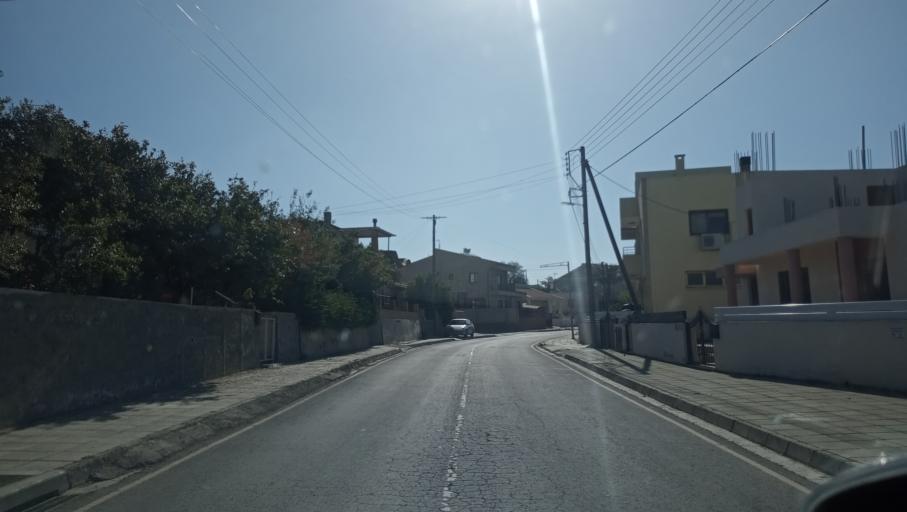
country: CY
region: Lefkosia
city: Tseri
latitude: 35.0759
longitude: 33.3283
